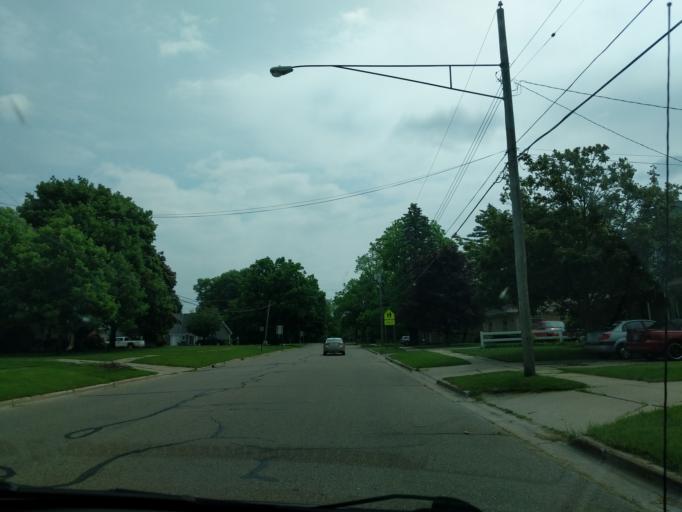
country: US
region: Michigan
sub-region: Ingham County
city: Williamston
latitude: 42.6937
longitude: -84.2756
